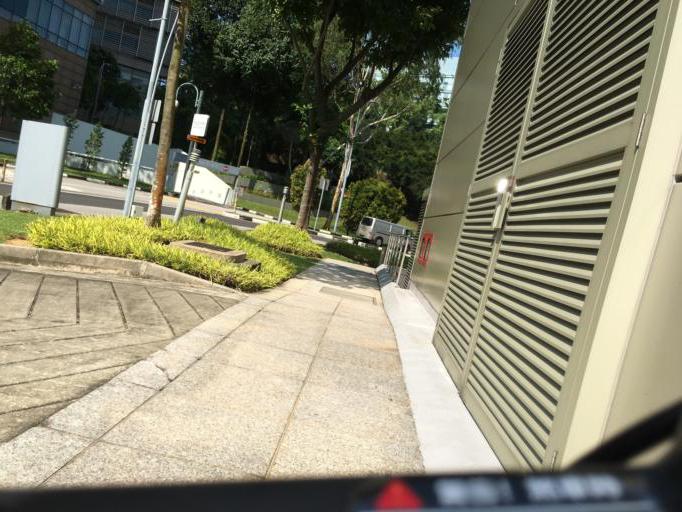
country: SG
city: Singapore
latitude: 1.3051
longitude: 103.7915
